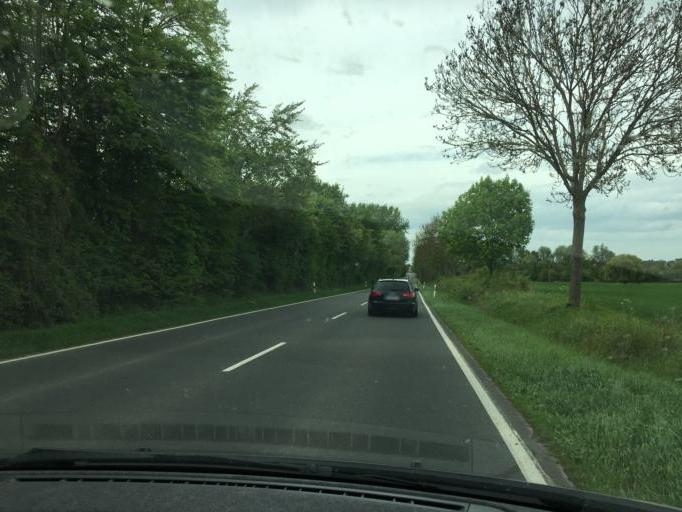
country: DE
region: North Rhine-Westphalia
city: Zulpich
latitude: 50.6982
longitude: 6.7206
